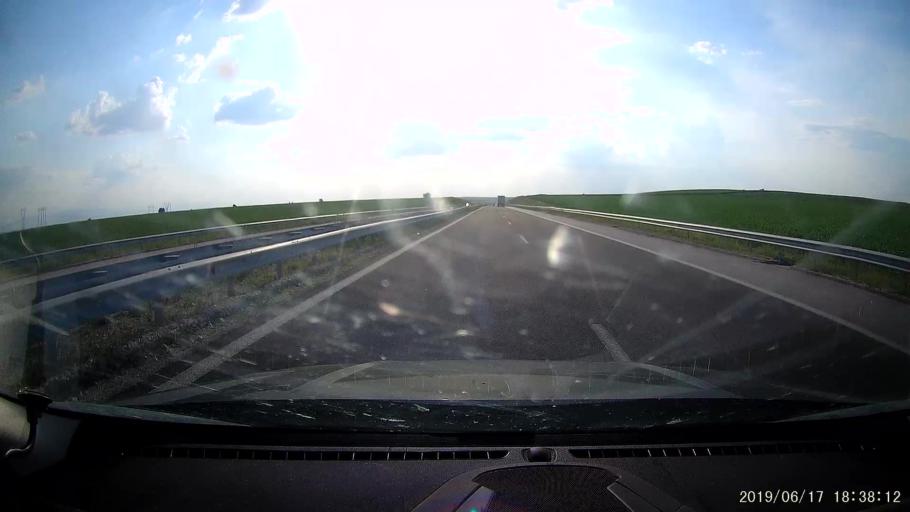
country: BG
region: Stara Zagora
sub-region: Obshtina Chirpan
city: Chirpan
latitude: 42.1356
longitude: 25.3430
